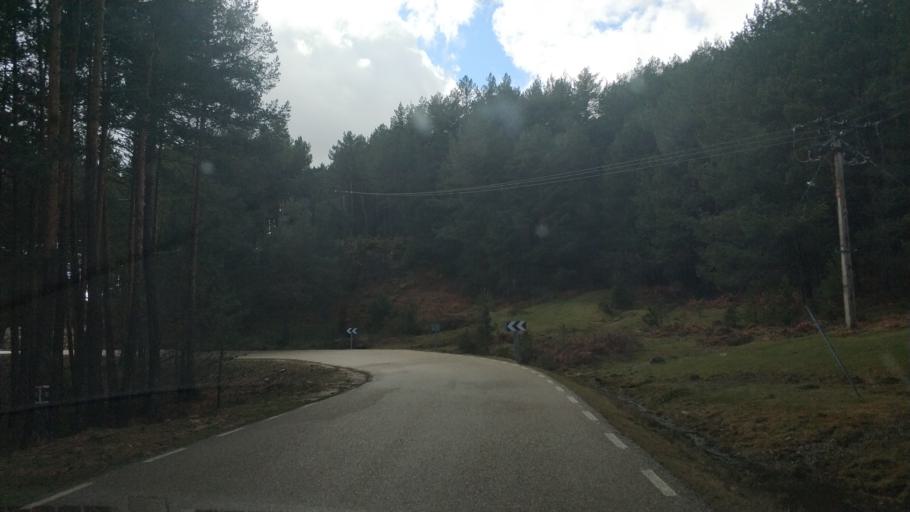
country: ES
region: Castille and Leon
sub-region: Provincia de Burgos
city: Neila
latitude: 42.0246
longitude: -3.0133
